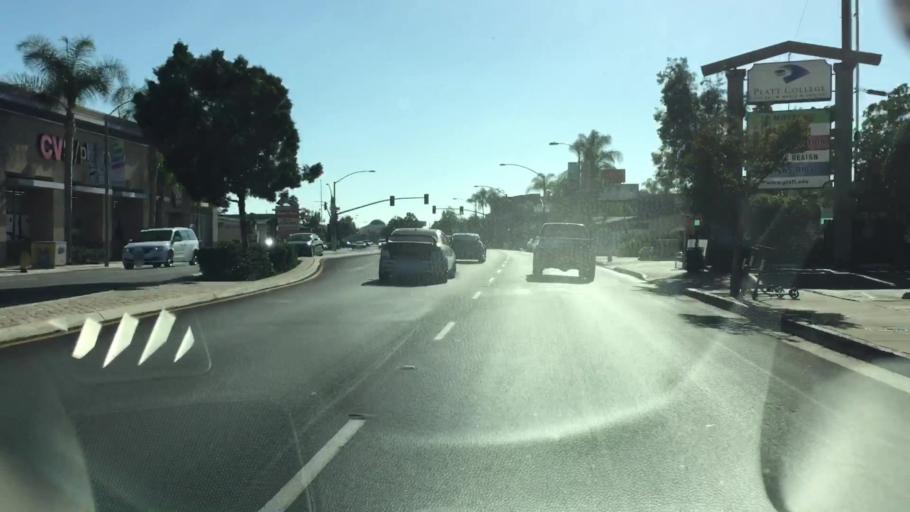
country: US
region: California
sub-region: San Diego County
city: Lemon Grove
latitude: 32.7636
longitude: -117.0635
